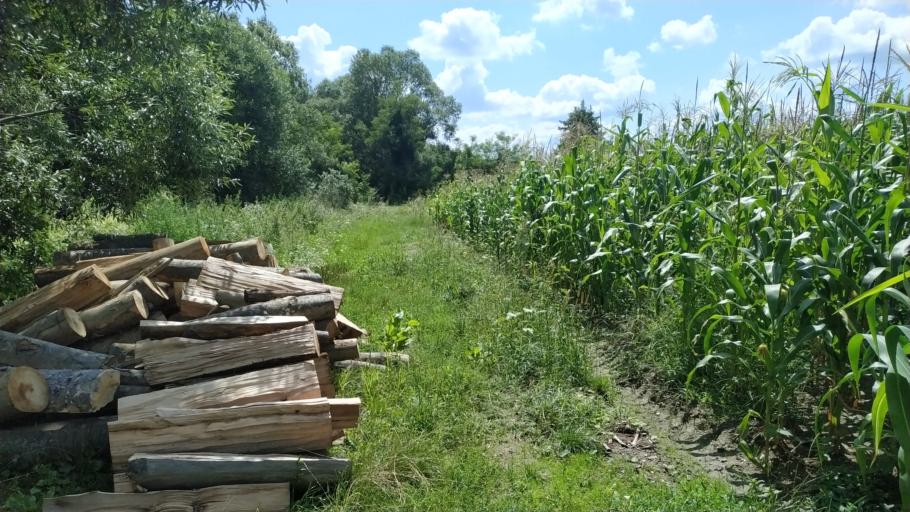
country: RO
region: Brasov
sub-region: Comuna Beclean
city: Beclean
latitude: 45.8284
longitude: 24.9225
